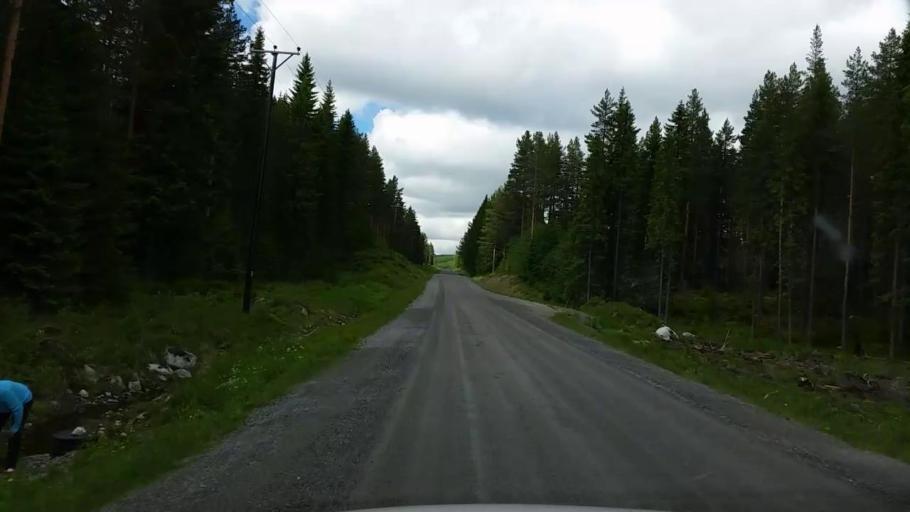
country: SE
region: Gaevleborg
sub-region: Bollnas Kommun
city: Vittsjo
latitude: 61.0835
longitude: 16.2559
